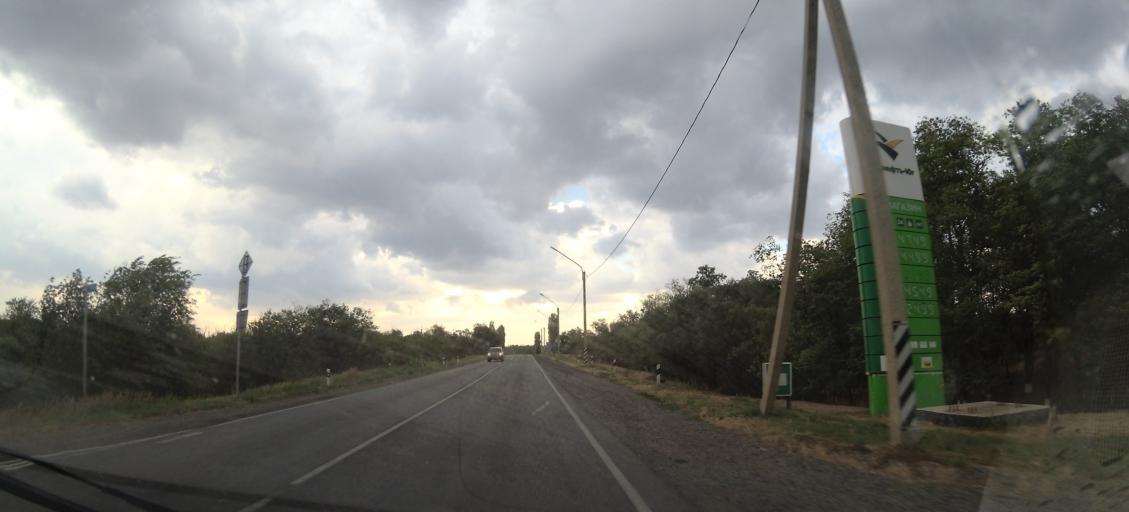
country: RU
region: Rostov
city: Orlovskiy
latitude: 46.8849
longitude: 42.0370
